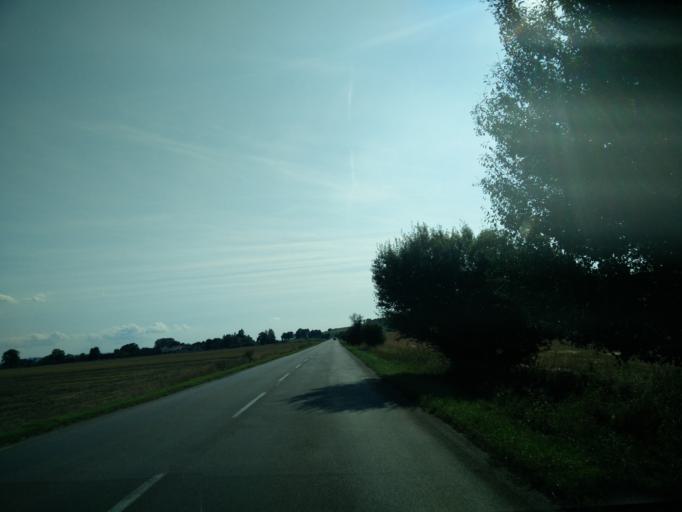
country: SK
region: Zilinsky
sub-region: Okres Martin
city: Martin
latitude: 48.9874
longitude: 18.8625
